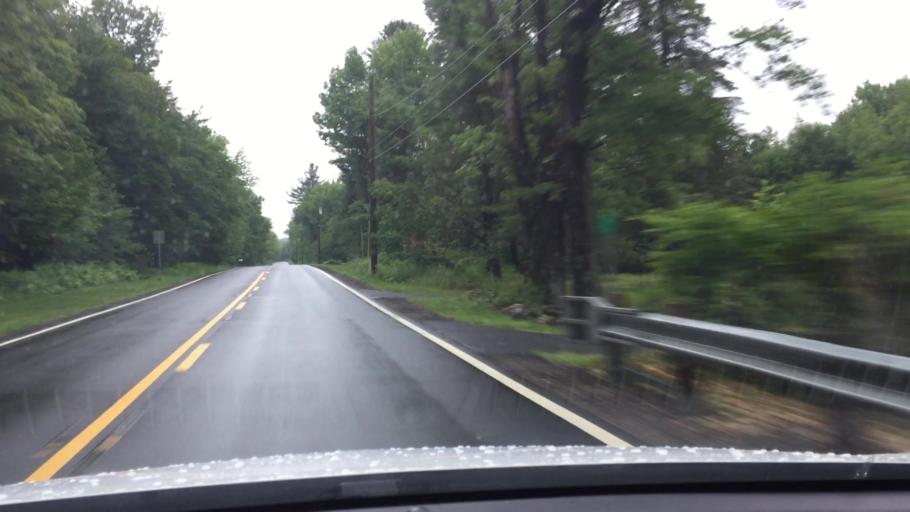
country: US
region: Massachusetts
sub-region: Berkshire County
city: Becket
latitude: 42.3505
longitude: -73.1254
